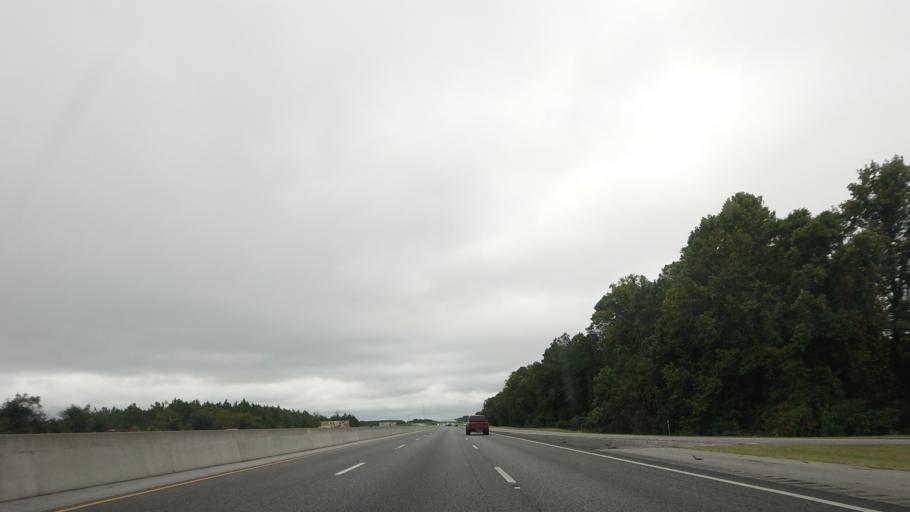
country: US
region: Georgia
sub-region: Turner County
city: Ashburn
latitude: 31.6339
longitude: -83.5823
